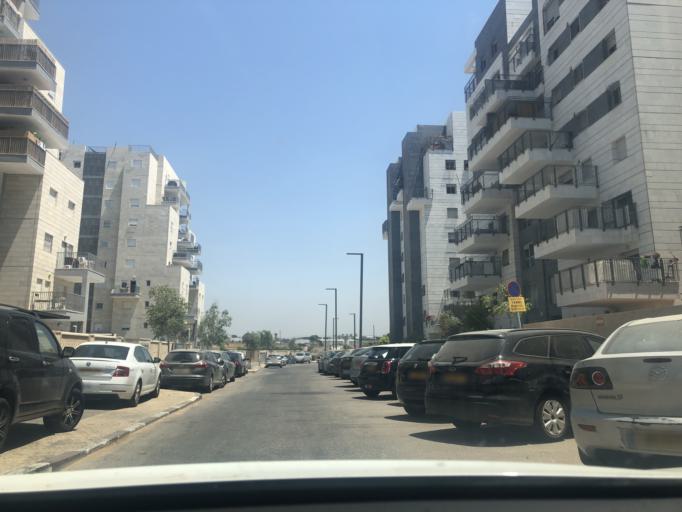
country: IL
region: Central District
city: Lod
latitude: 31.9364
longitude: 34.8986
